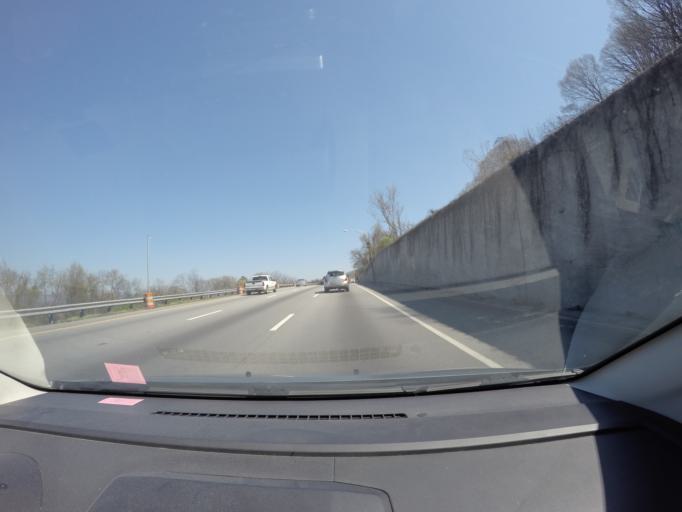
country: US
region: Tennessee
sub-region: Hamilton County
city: East Ridge
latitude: 35.0173
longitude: -85.2685
